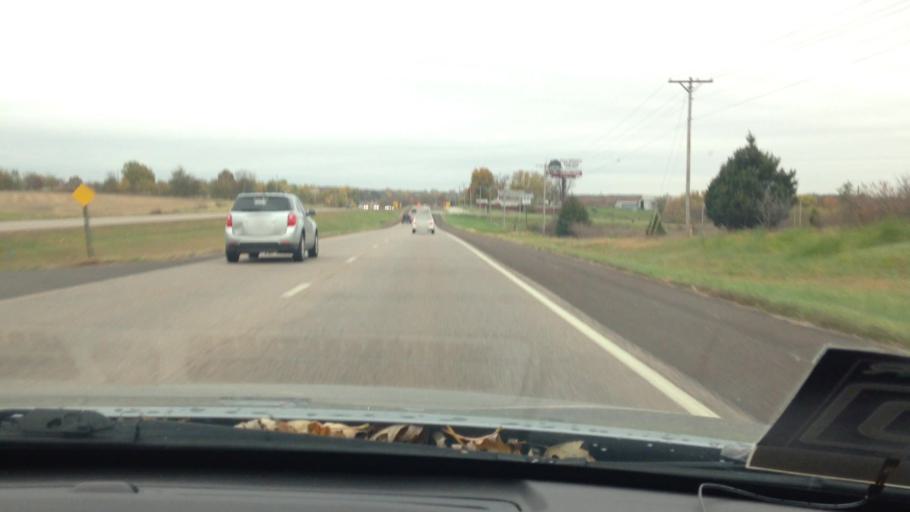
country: US
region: Kansas
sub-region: Leavenworth County
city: Basehor
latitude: 39.1536
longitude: -94.9009
